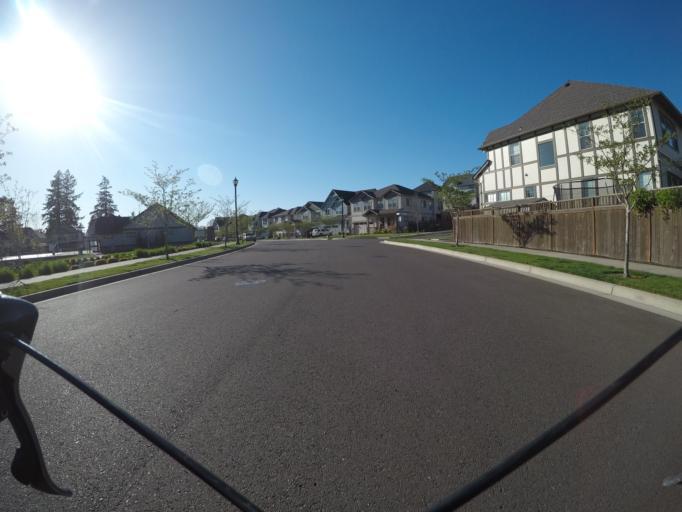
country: US
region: Oregon
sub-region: Washington County
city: King City
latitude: 45.4232
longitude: -122.8552
